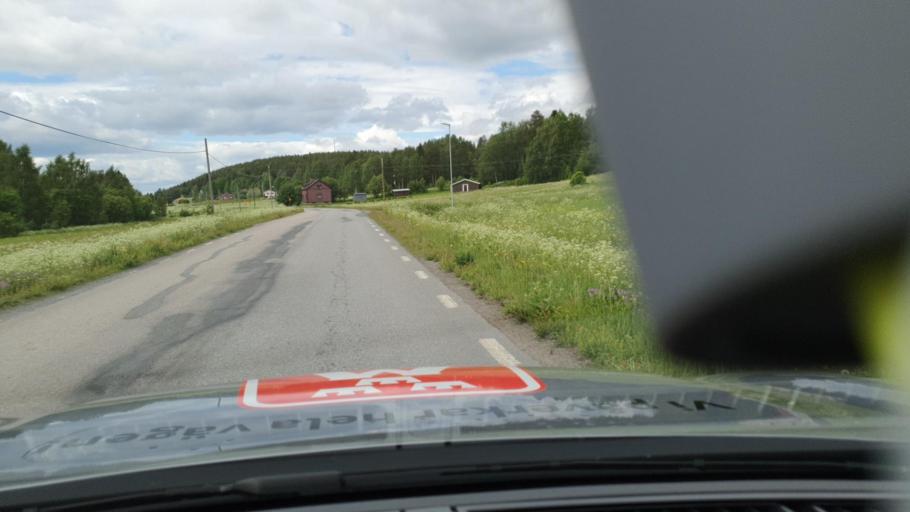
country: SE
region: Norrbotten
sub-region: Bodens Kommun
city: Saevast
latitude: 65.8696
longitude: 21.8945
